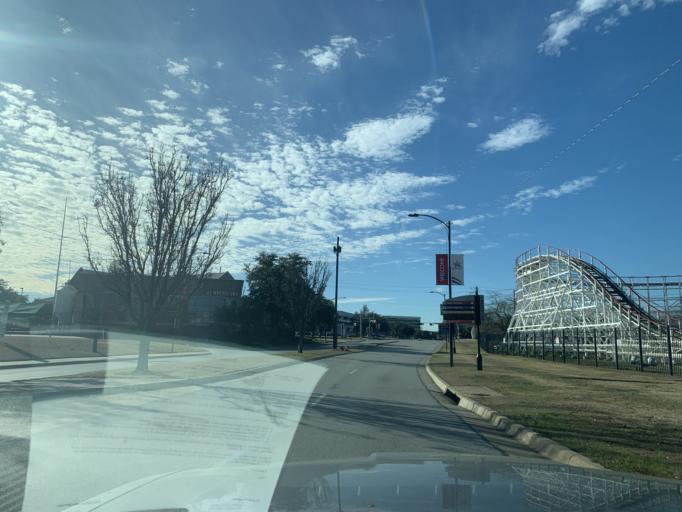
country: US
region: Texas
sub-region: Tarrant County
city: Arlington
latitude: 32.7538
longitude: -97.0675
